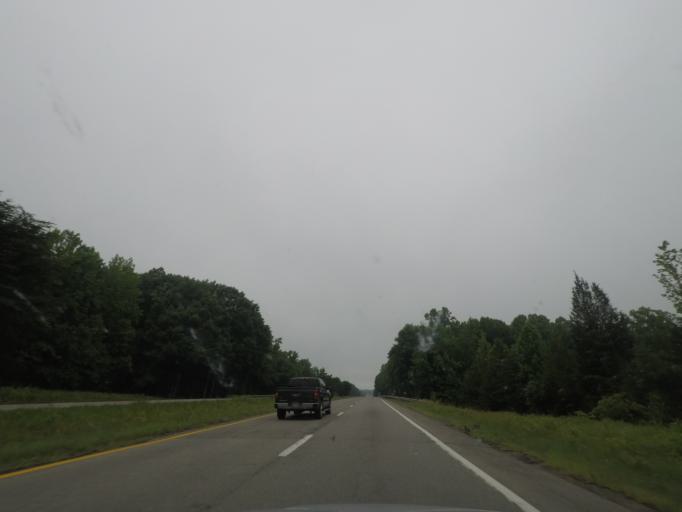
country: US
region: Virginia
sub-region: Charlotte County
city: Charlotte Court House
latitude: 37.0474
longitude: -78.4703
